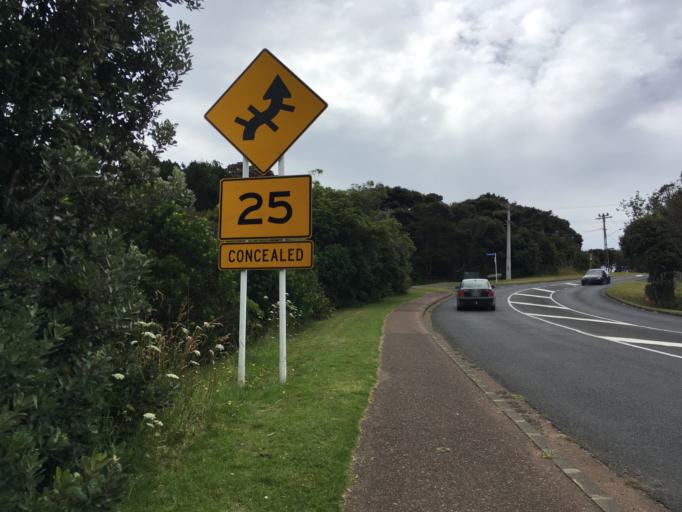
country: NZ
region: Auckland
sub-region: Auckland
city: Pakuranga
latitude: -36.7891
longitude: 175.0233
